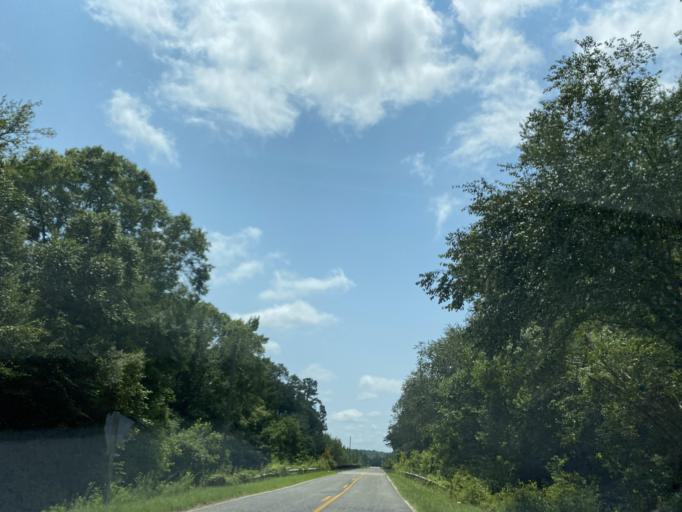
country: US
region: Georgia
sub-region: Telfair County
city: Lumber City
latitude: 31.9740
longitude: -82.7043
